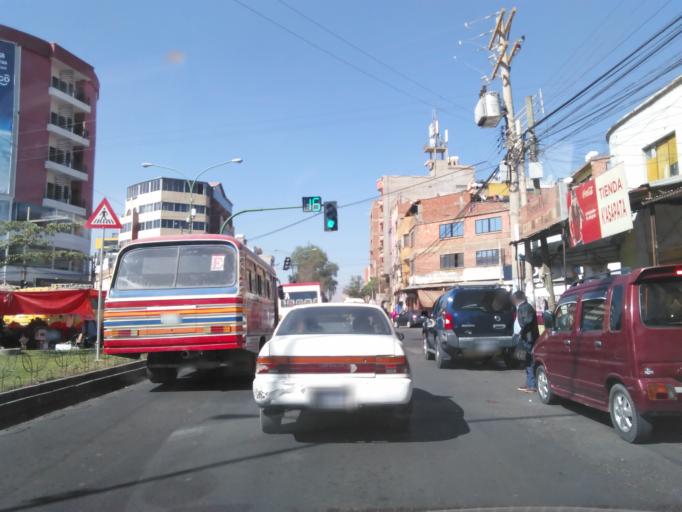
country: BO
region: Cochabamba
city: Cochabamba
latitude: -17.4072
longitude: -66.1567
